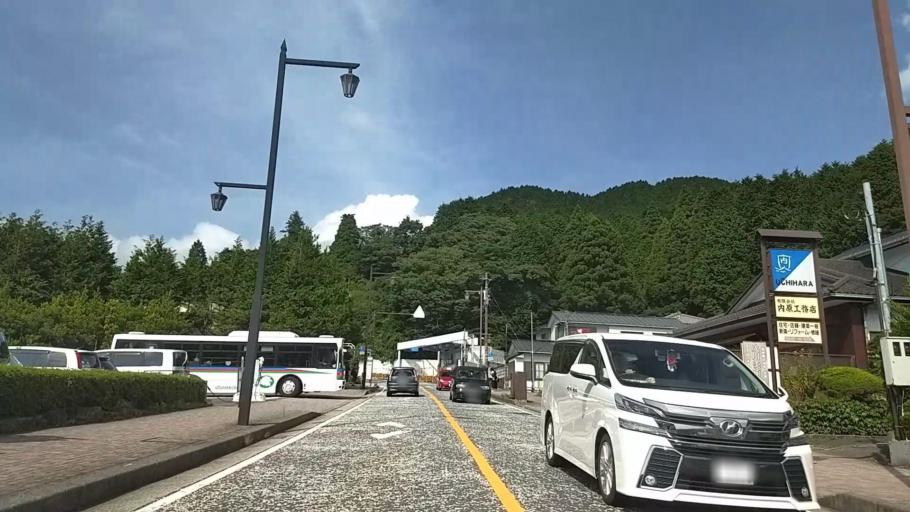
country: JP
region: Kanagawa
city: Hakone
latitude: 35.1910
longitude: 139.0270
